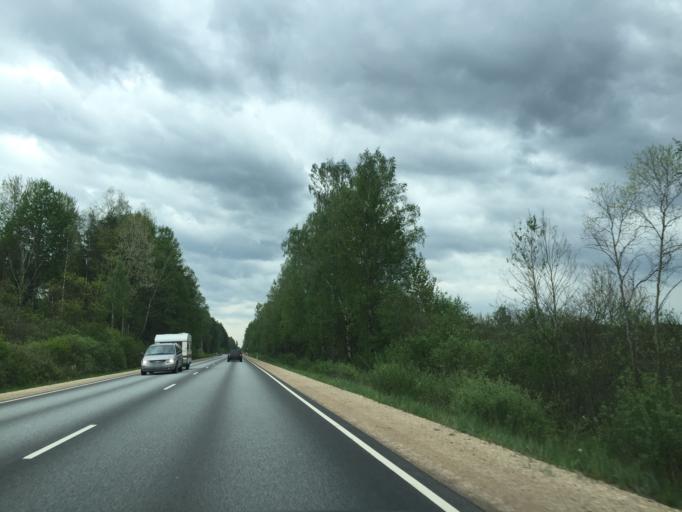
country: LV
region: Ikskile
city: Ikskile
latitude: 56.8795
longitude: 24.5150
